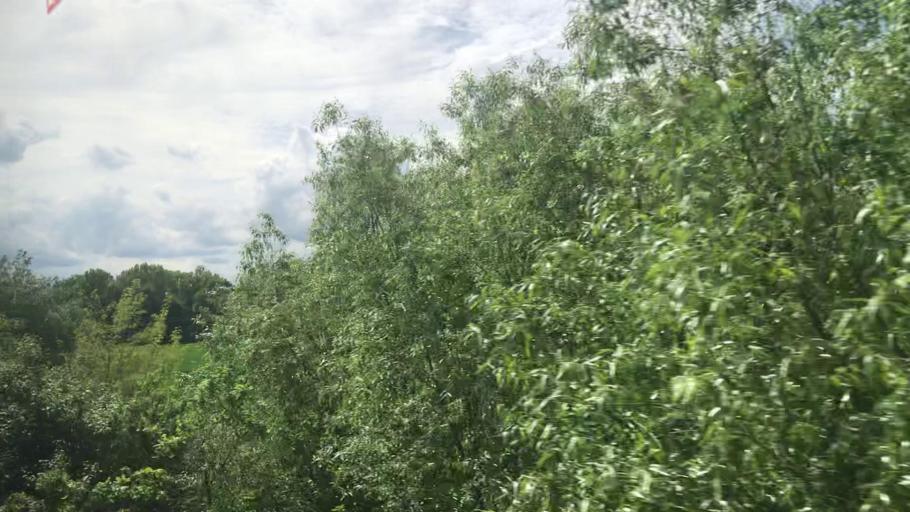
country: PL
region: Lower Silesian Voivodeship
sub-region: Powiat swidnicki
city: Jaworzyna Slaska
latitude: 50.8932
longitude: 16.3994
